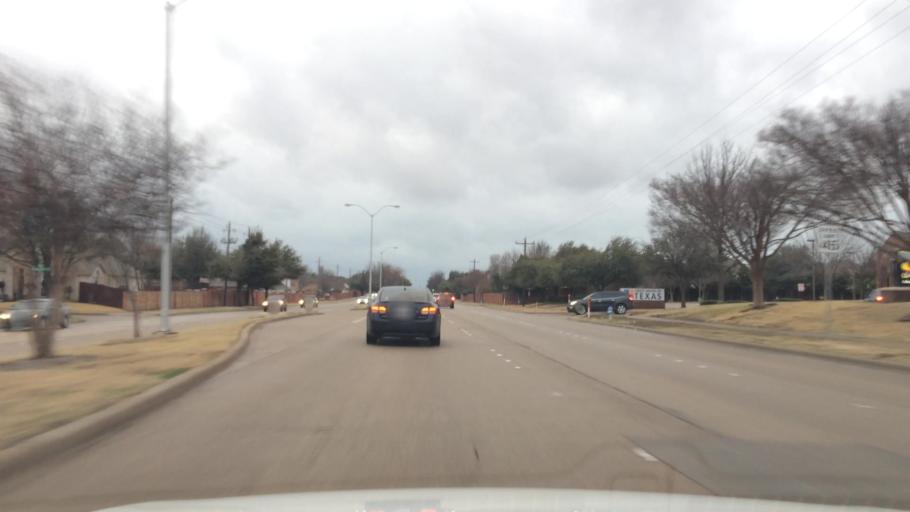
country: US
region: Texas
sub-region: Collin County
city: Frisco
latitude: 33.0852
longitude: -96.7718
